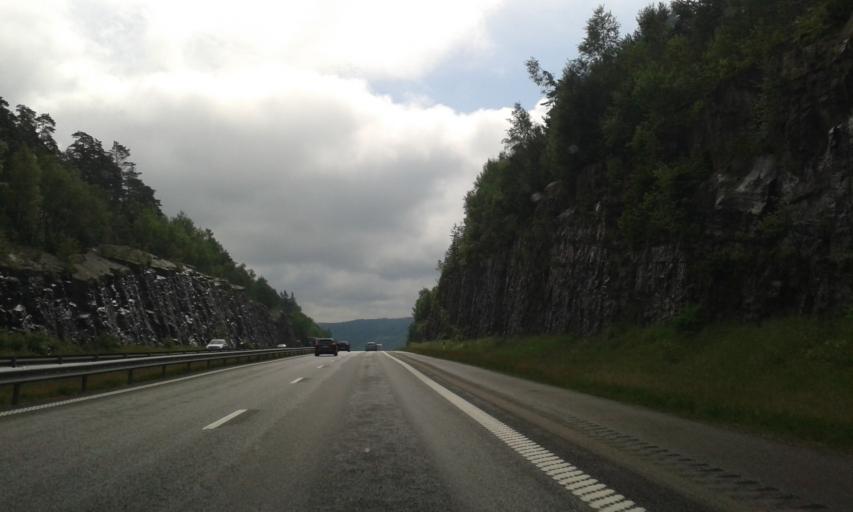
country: SE
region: Vaestra Goetaland
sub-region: Harryda Kommun
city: Ravlanda
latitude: 57.6701
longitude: 12.5202
